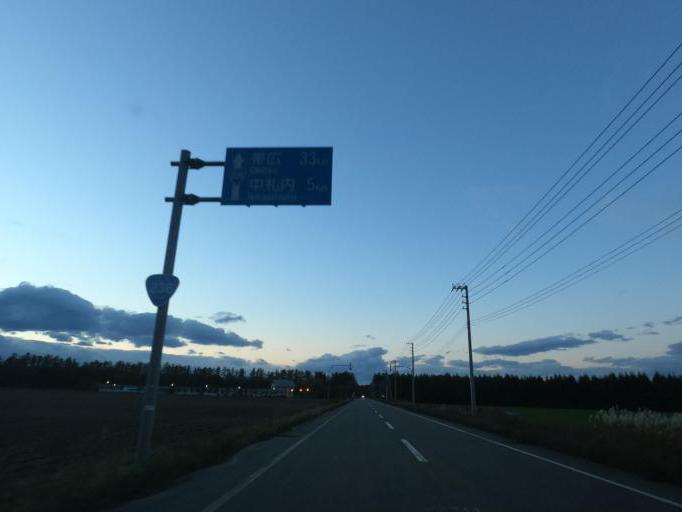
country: JP
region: Hokkaido
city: Obihiro
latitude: 42.6711
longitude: 143.1704
